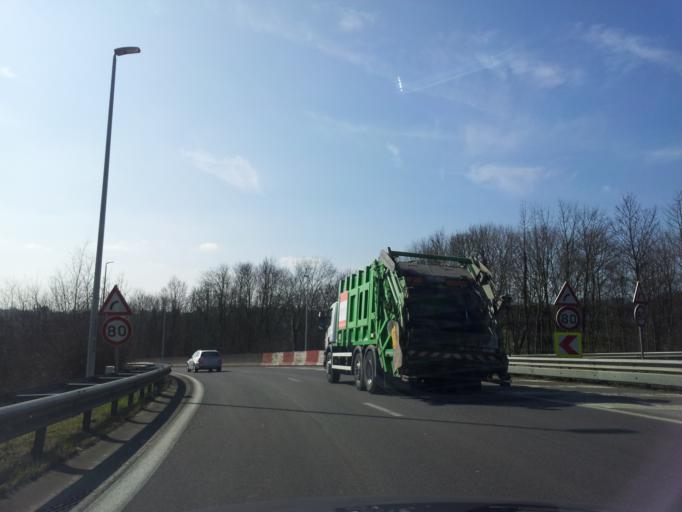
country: BE
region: Wallonia
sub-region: Province de Liege
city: Dison
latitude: 50.6393
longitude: 5.8342
